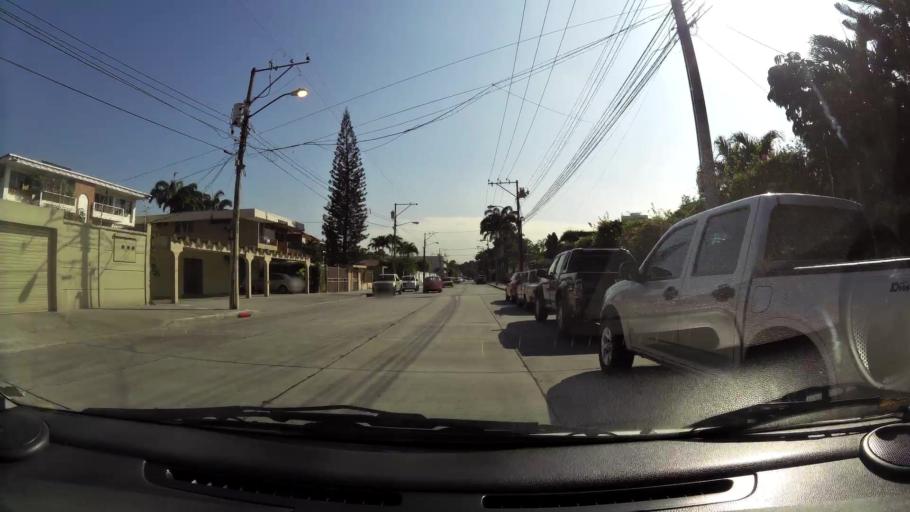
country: EC
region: Guayas
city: Guayaquil
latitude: -2.1720
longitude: -79.9031
